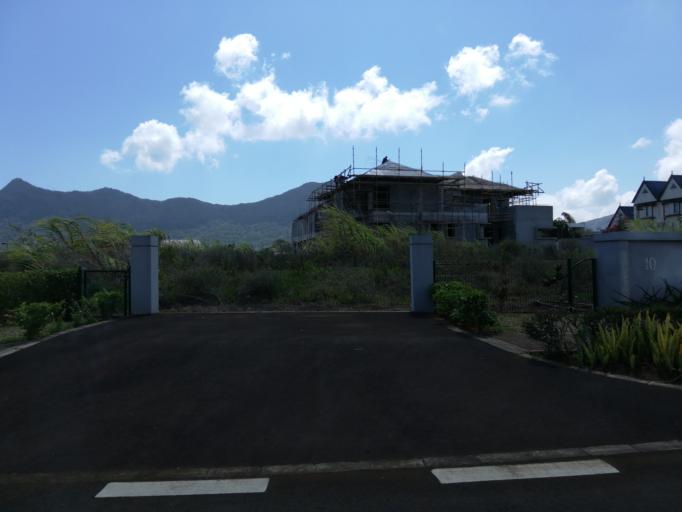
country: MU
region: Moka
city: Saint Pierre
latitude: -20.2289
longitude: 57.5108
